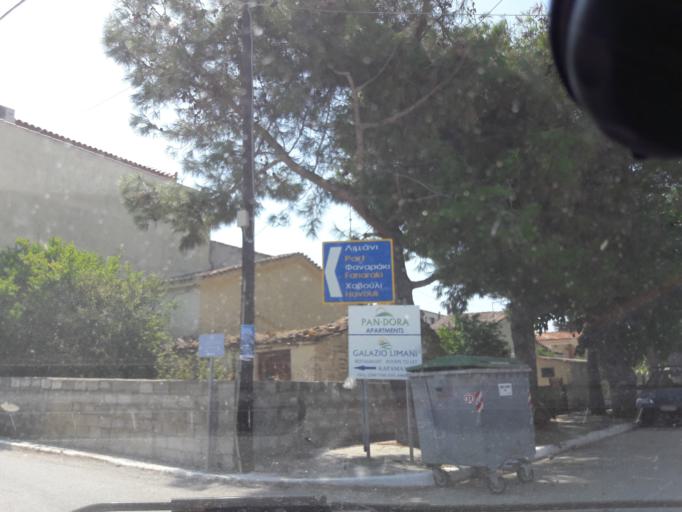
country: GR
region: North Aegean
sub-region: Nomos Lesvou
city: Myrina
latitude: 39.8770
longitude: 25.2706
